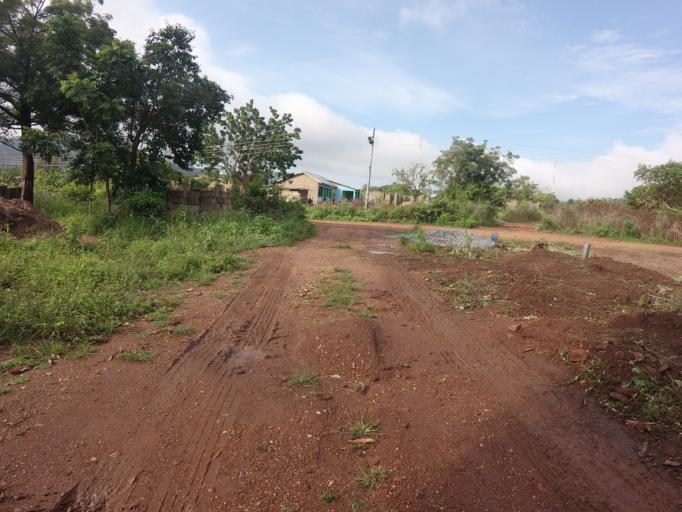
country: GH
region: Volta
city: Ho
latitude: 6.5350
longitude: 0.2293
